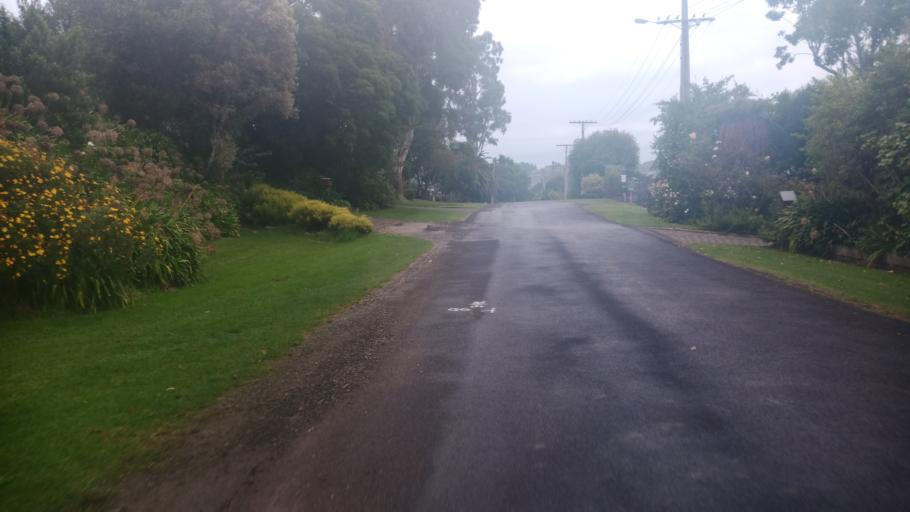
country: NZ
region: Gisborne
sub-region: Gisborne District
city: Gisborne
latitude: -38.6639
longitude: 178.0414
